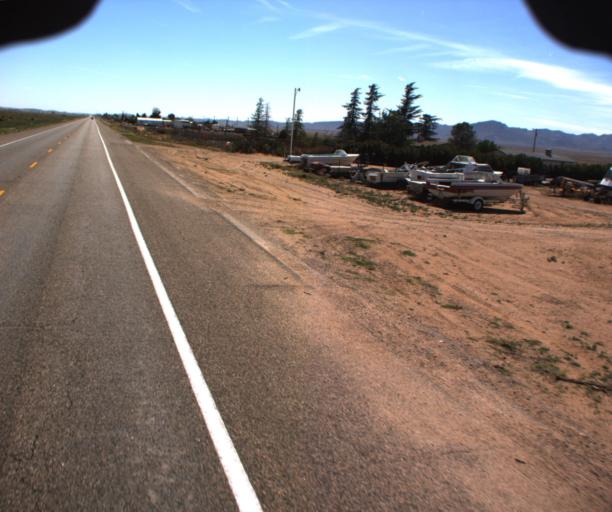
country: US
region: Arizona
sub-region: Mohave County
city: New Kingman-Butler
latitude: 35.3066
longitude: -113.9253
